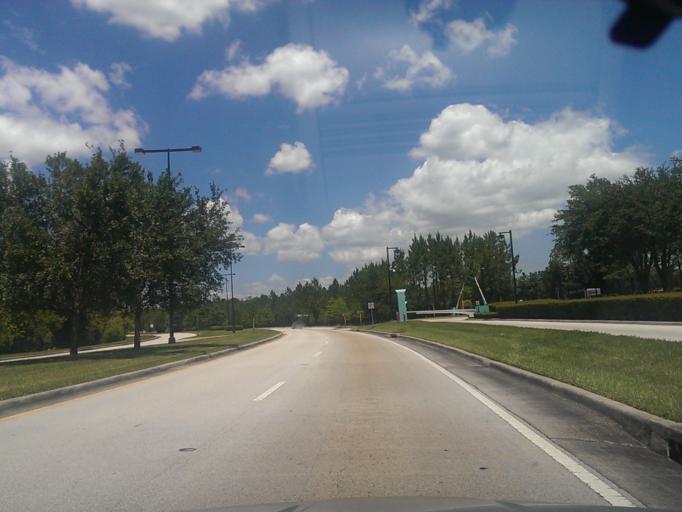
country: US
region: Florida
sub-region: Osceola County
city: Celebration
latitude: 28.3597
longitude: -81.5747
